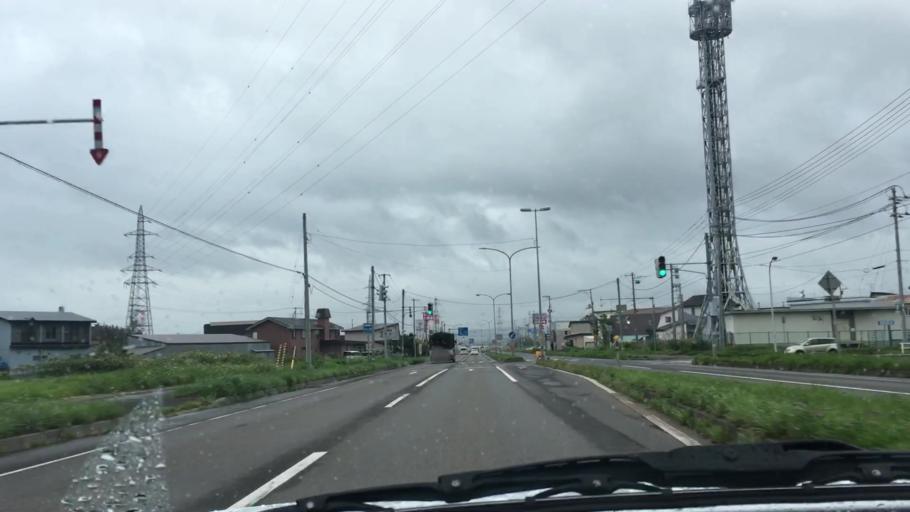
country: JP
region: Hokkaido
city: Nanae
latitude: 42.2586
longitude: 140.2780
